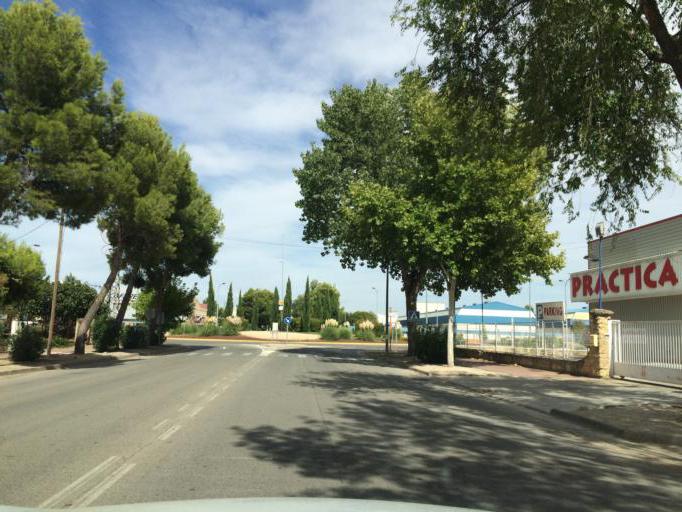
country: ES
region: Castille-La Mancha
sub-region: Provincia de Albacete
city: Albacete
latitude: 39.0173
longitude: -1.8835
